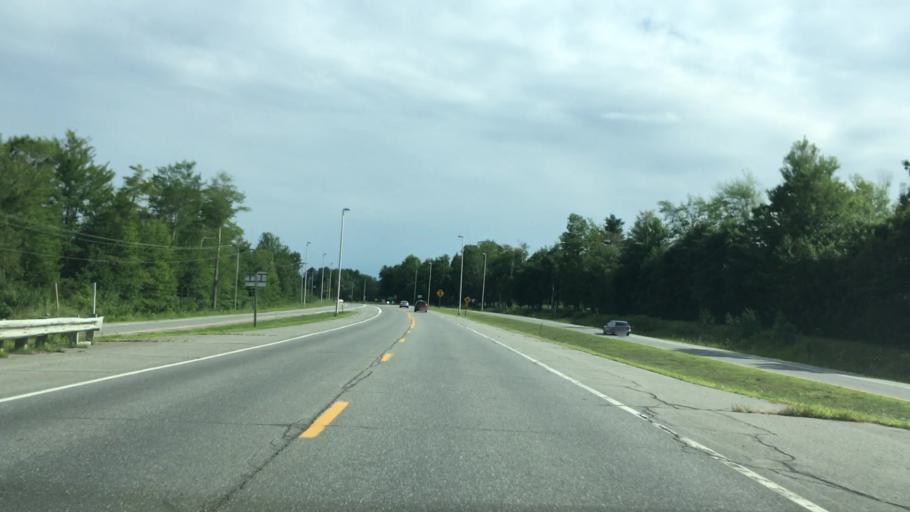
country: US
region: Maine
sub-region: Waldo County
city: Belfast
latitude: 44.4216
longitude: -69.0210
